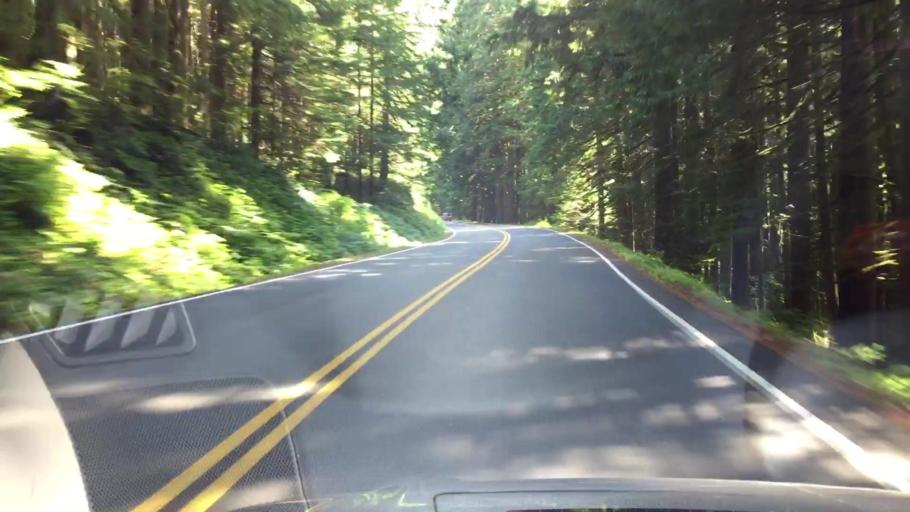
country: US
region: Washington
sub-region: Pierce County
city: Eatonville
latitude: 46.7384
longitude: -121.8782
